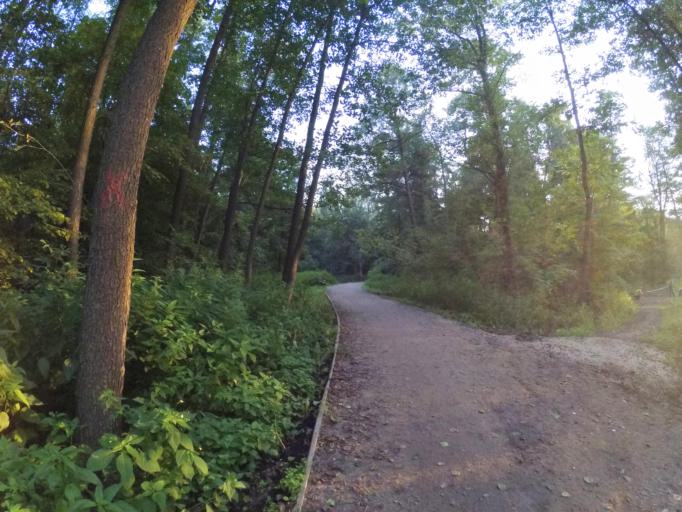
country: RU
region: Moscow
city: Vykhino-Zhulebino
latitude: 55.6873
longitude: 37.8106
